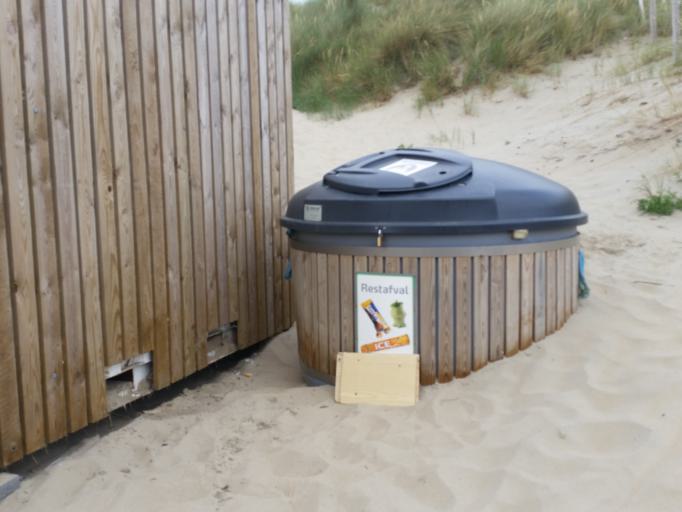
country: BE
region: Flanders
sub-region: Provincie West-Vlaanderen
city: Bredene
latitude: 51.2495
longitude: 2.9604
